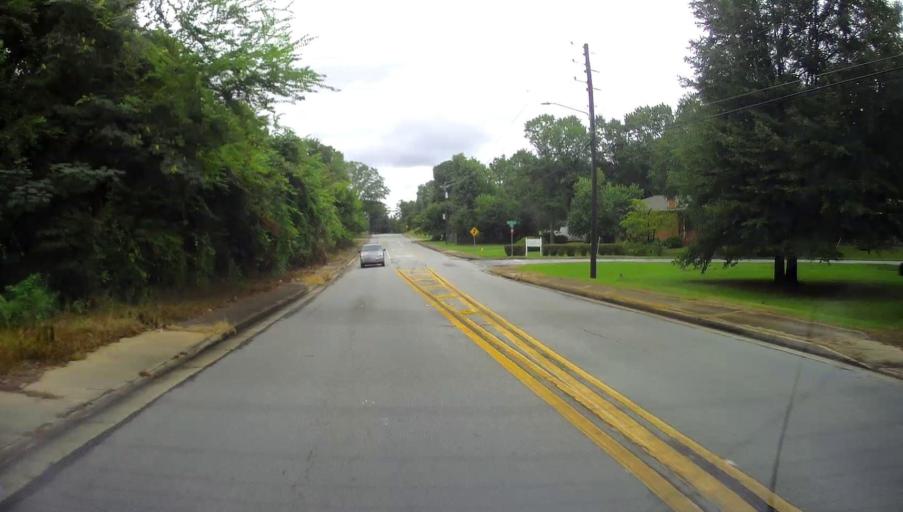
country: US
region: Georgia
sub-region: Bibb County
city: Macon
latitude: 32.7949
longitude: -83.6972
